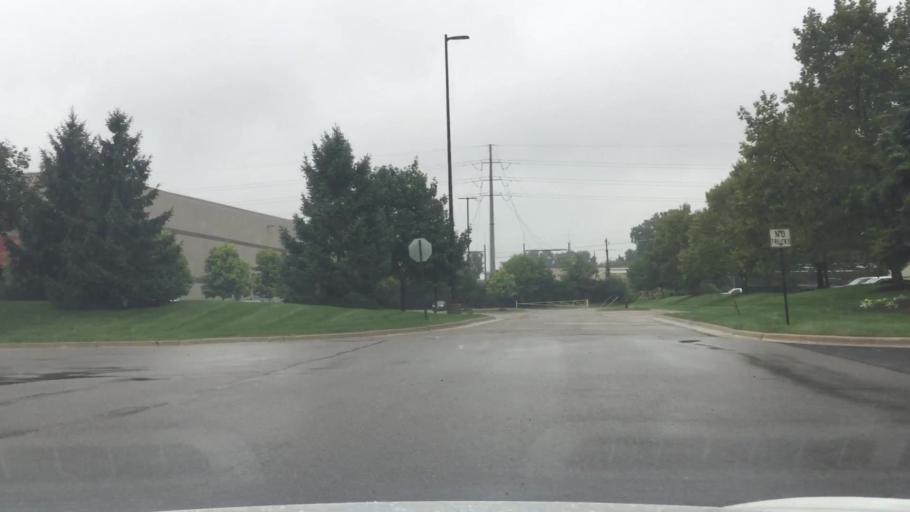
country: US
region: Michigan
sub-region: Wayne County
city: Livonia
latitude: 42.3781
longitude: -83.3266
